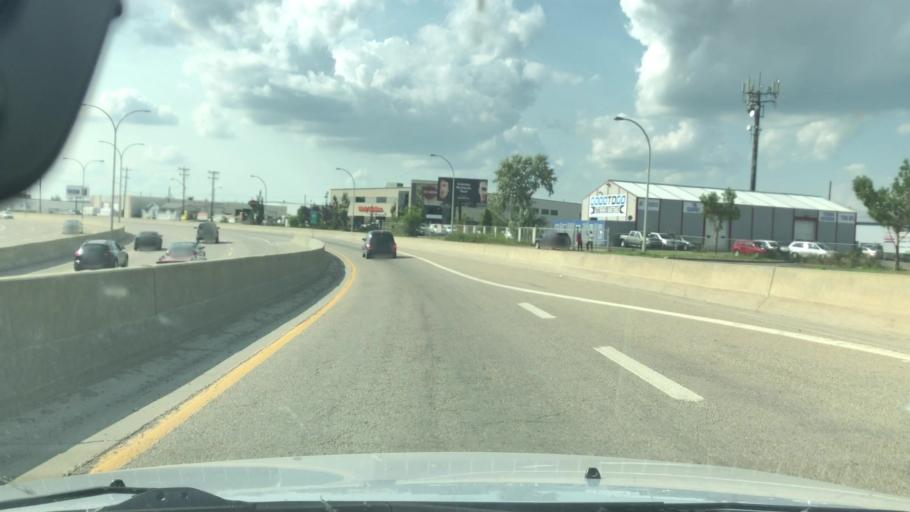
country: CA
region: Alberta
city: Edmonton
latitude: 53.5817
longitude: -113.4541
